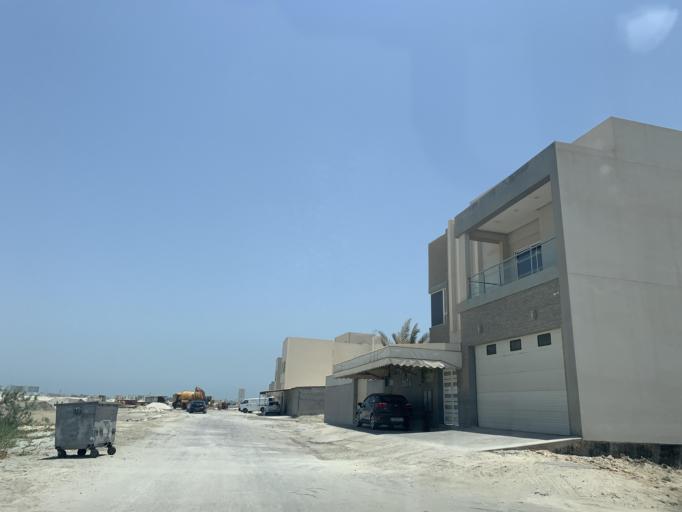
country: BH
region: Muharraq
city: Al Muharraq
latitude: 26.2874
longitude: 50.6193
